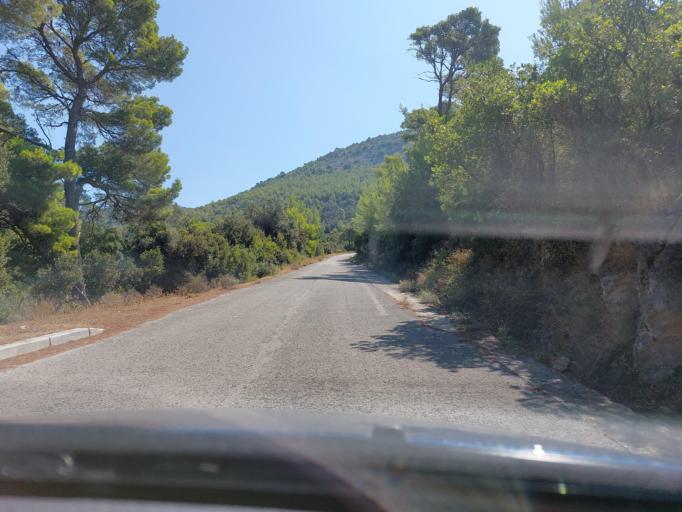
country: HR
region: Dubrovacko-Neretvanska
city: Smokvica
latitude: 42.7491
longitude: 16.8442
